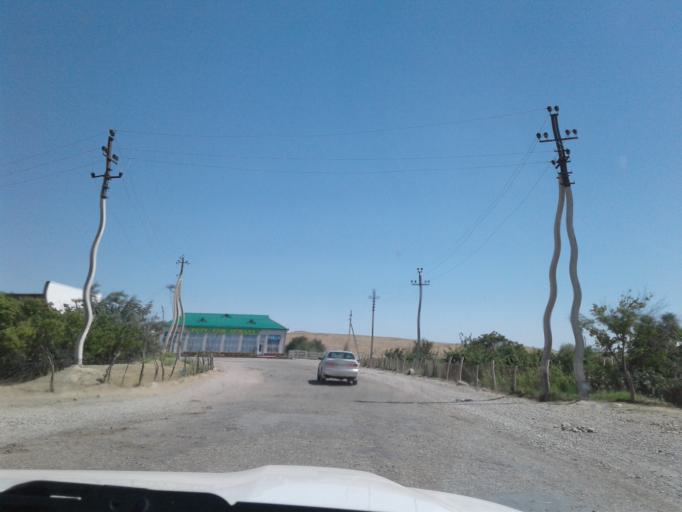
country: AF
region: Badghis
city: Bala Murghab
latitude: 35.9549
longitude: 62.9054
